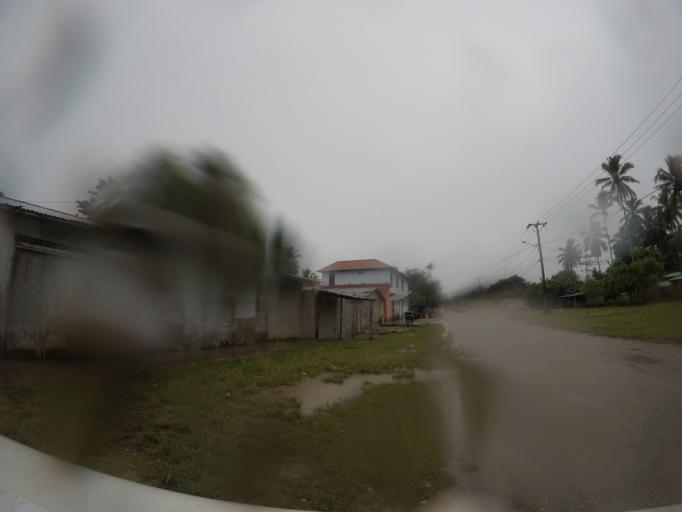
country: TL
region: Lautem
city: Lospalos
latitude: -8.5214
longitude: 126.9993
